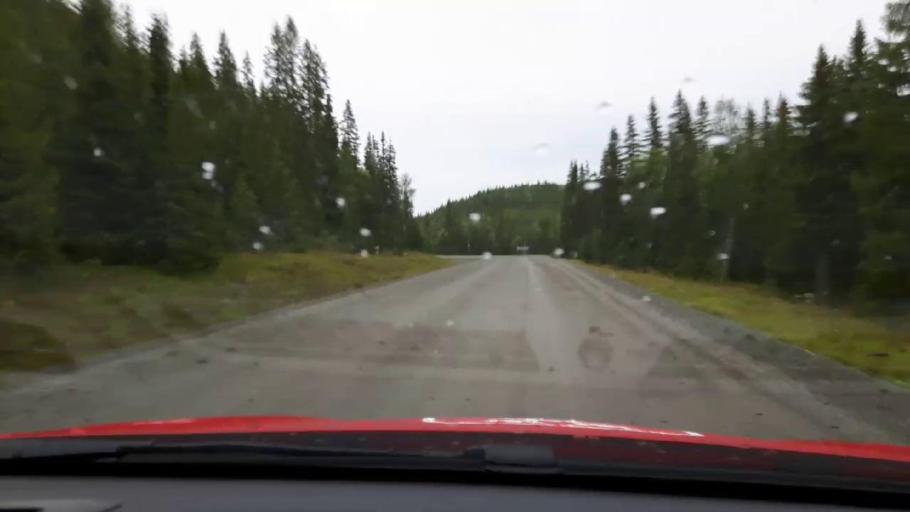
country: SE
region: Jaemtland
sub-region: Are Kommun
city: Are
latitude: 63.4242
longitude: 12.7414
